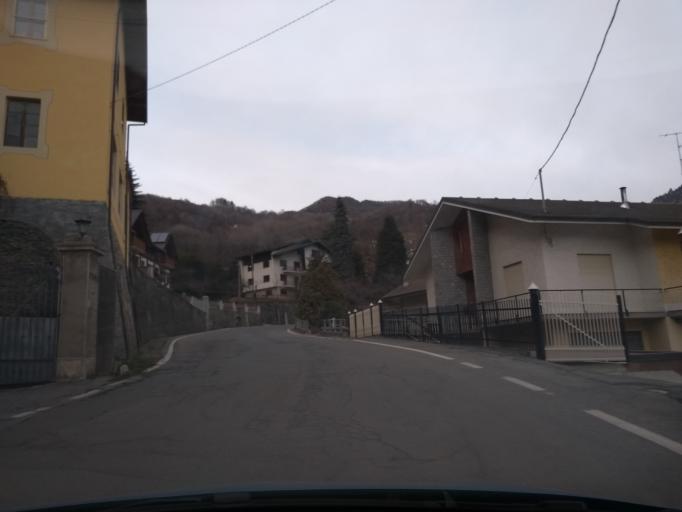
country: IT
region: Piedmont
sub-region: Provincia di Torino
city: Viu
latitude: 45.2363
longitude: 7.3712
